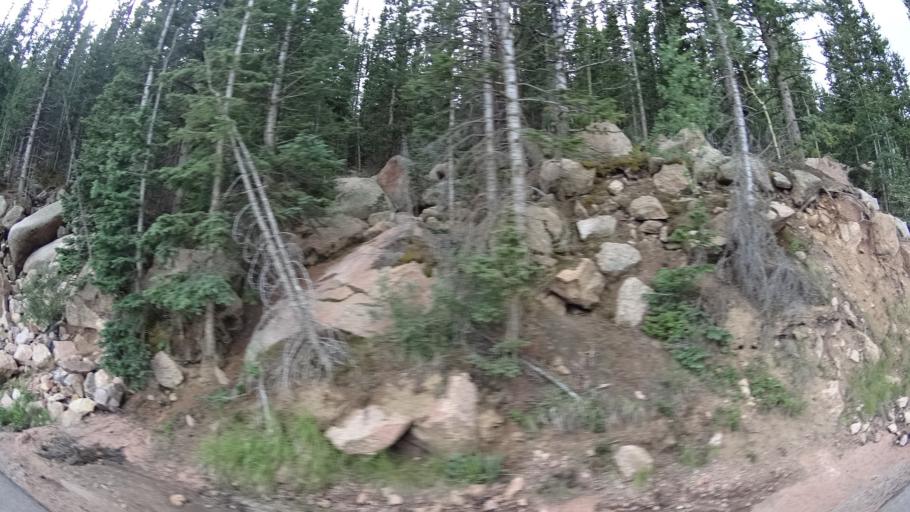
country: US
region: Colorado
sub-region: El Paso County
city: Cascade-Chipita Park
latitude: 38.8909
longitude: -105.0671
